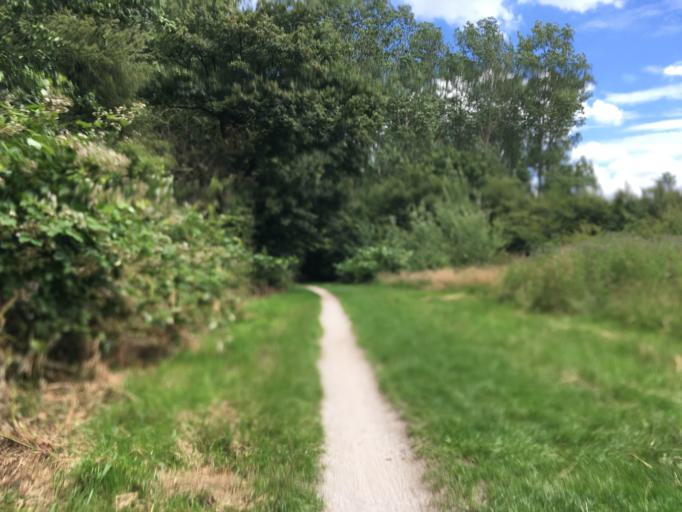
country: NL
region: North Holland
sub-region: Gemeente Velsen
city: Velsen-Zuid
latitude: 52.4191
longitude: 4.7013
